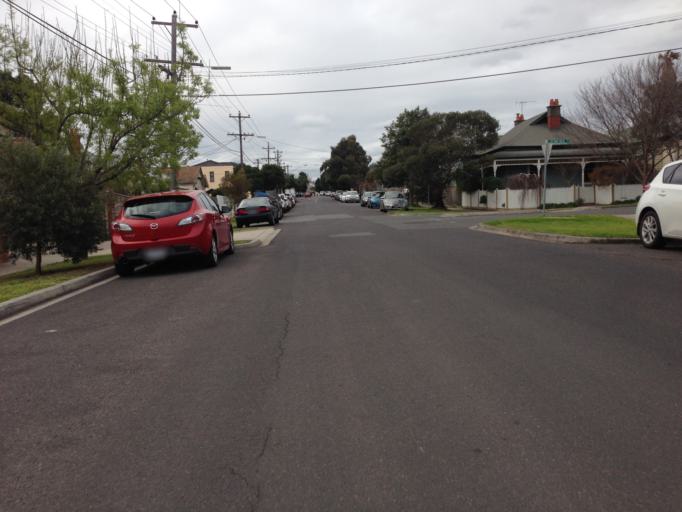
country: AU
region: Victoria
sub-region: Darebin
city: Northcote
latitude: -37.7651
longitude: 145.0052
